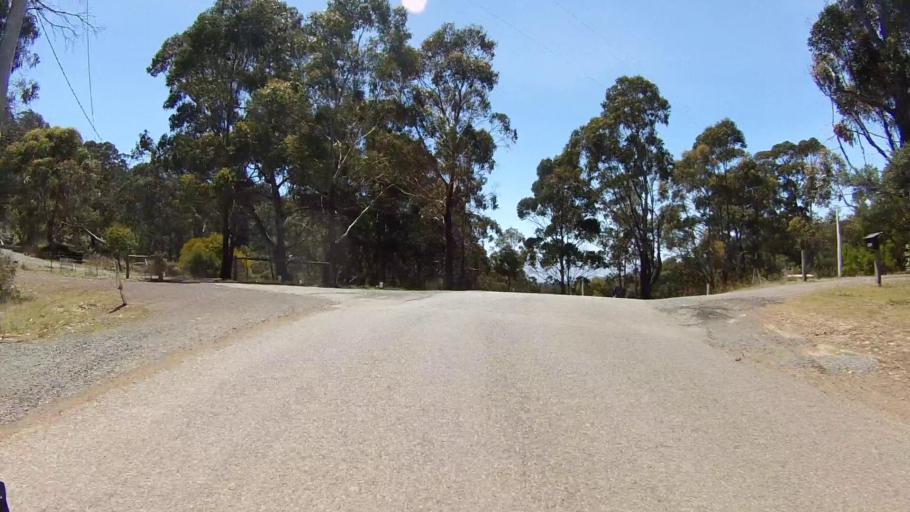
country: AU
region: Tasmania
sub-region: Clarence
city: Cambridge
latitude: -42.8520
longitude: 147.4319
